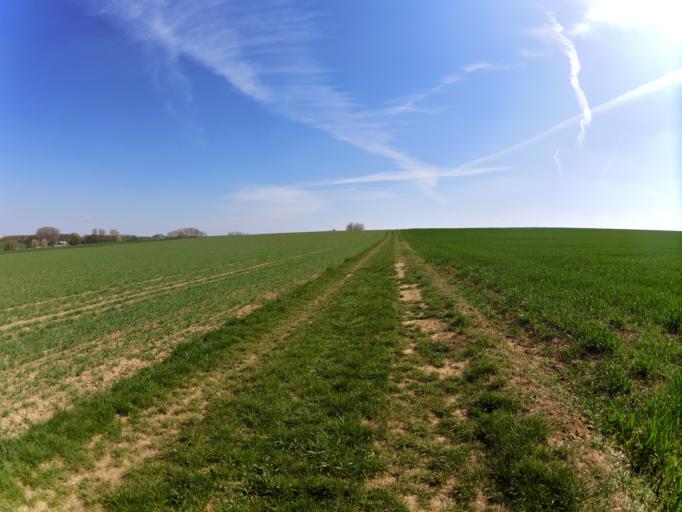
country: DE
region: Bavaria
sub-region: Regierungsbezirk Unterfranken
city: Kurnach
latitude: 49.8643
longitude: 10.0158
